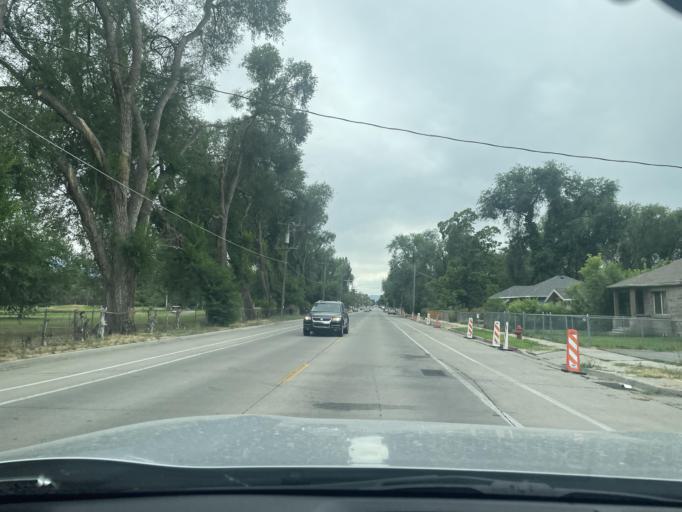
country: US
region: Utah
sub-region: Salt Lake County
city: South Salt Lake
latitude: 40.7111
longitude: -111.8769
